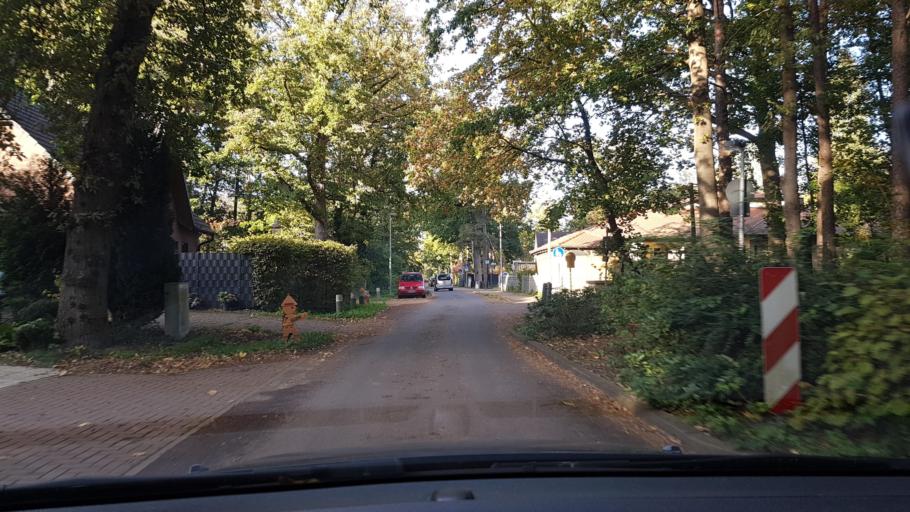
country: DE
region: Lower Saxony
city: Isernhagen Farster Bauerschaft
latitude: 52.5141
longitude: 9.7809
